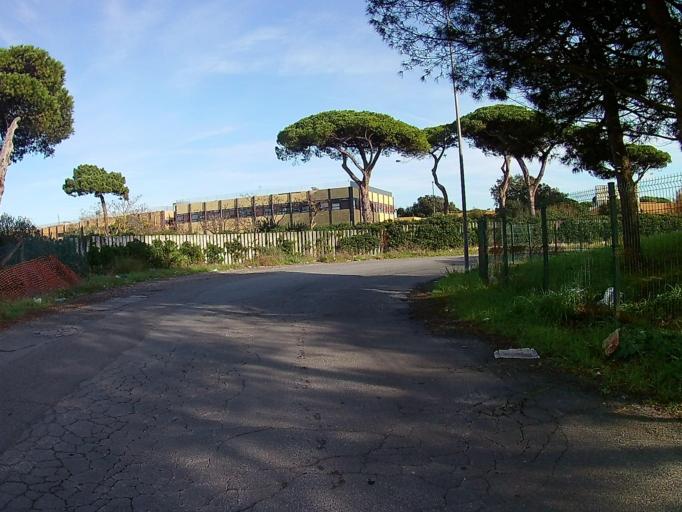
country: IT
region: Latium
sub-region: Citta metropolitana di Roma Capitale
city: Lido di Ostia
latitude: 41.7279
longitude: 12.2983
